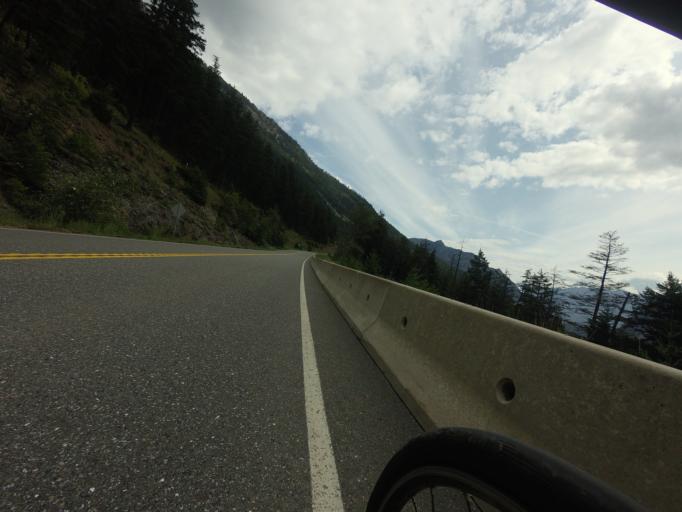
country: CA
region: British Columbia
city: Lillooet
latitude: 50.6436
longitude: -122.0234
